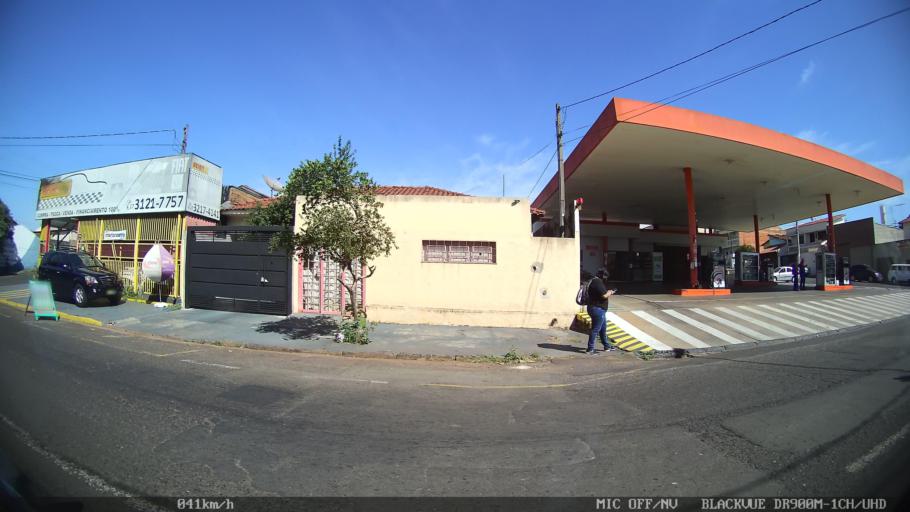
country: BR
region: Sao Paulo
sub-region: Sao Jose Do Rio Preto
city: Sao Jose do Rio Preto
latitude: -20.7767
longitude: -49.3967
